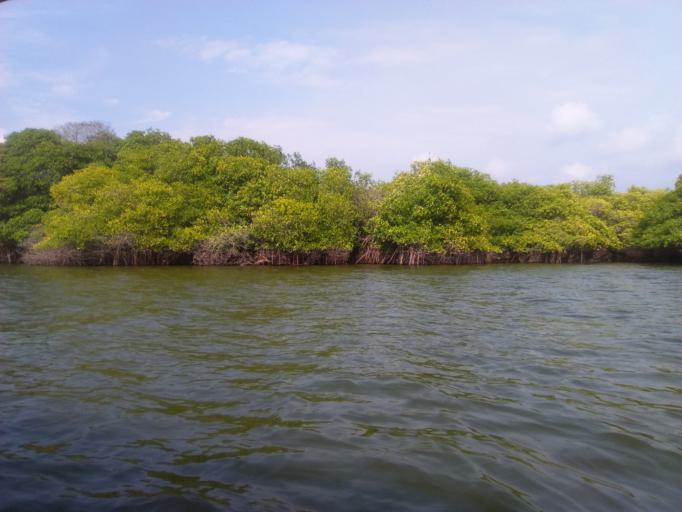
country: MX
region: Guerrero
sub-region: Coyuca de Benitez
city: Colonia Luces en el Mar
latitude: 16.9050
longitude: -99.9707
